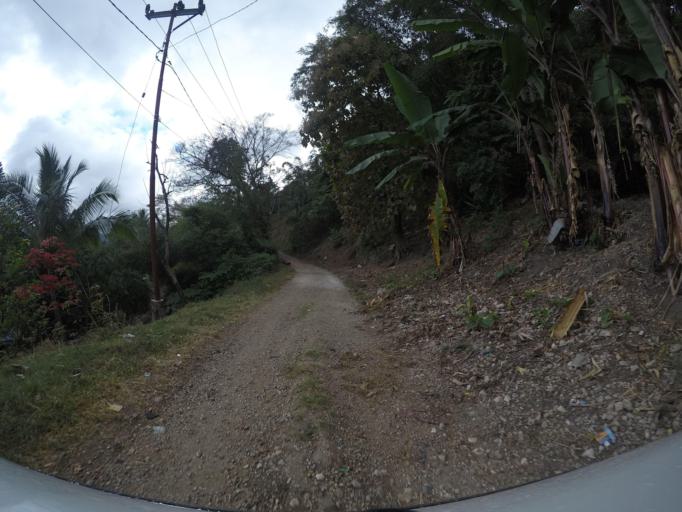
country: TL
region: Baucau
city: Baucau
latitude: -8.6442
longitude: 126.6337
